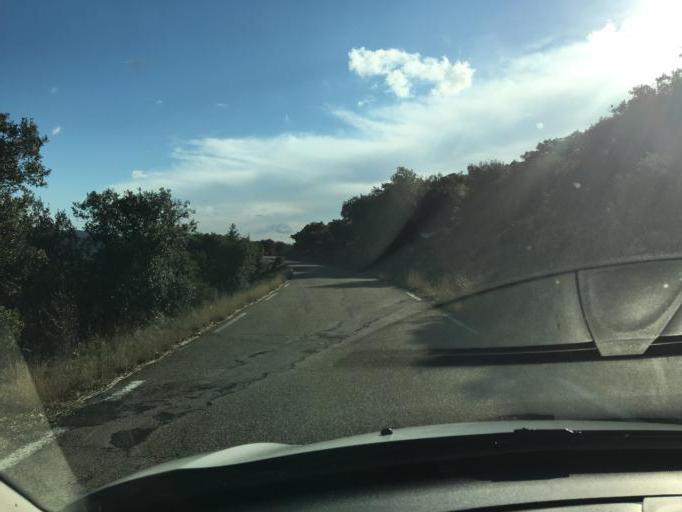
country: FR
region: Provence-Alpes-Cote d'Azur
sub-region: Departement du Vaucluse
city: Villes-sur-Auzon
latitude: 44.0440
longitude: 5.2533
